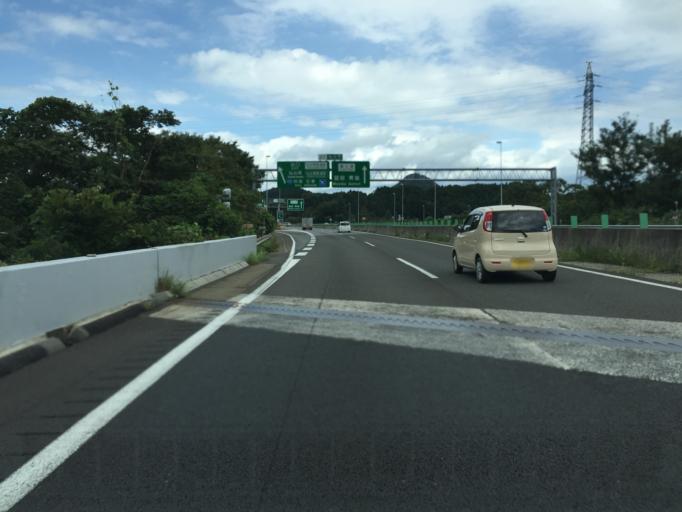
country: JP
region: Miyagi
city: Sendai
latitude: 38.2123
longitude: 140.8048
